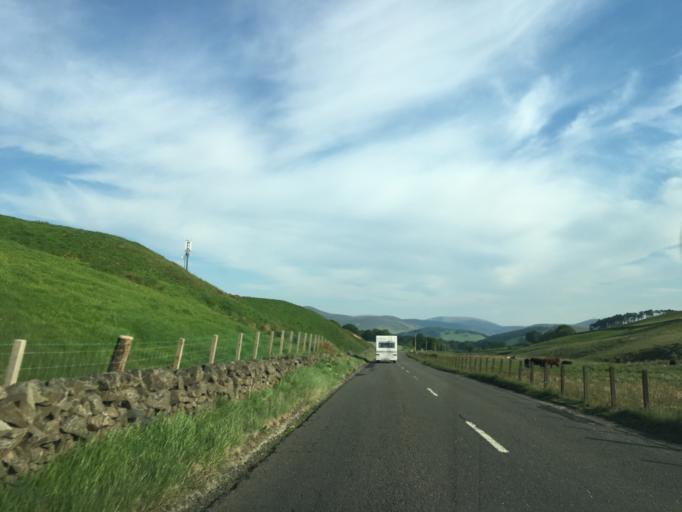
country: GB
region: Scotland
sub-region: South Lanarkshire
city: Biggar
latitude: 55.6327
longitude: -3.4208
